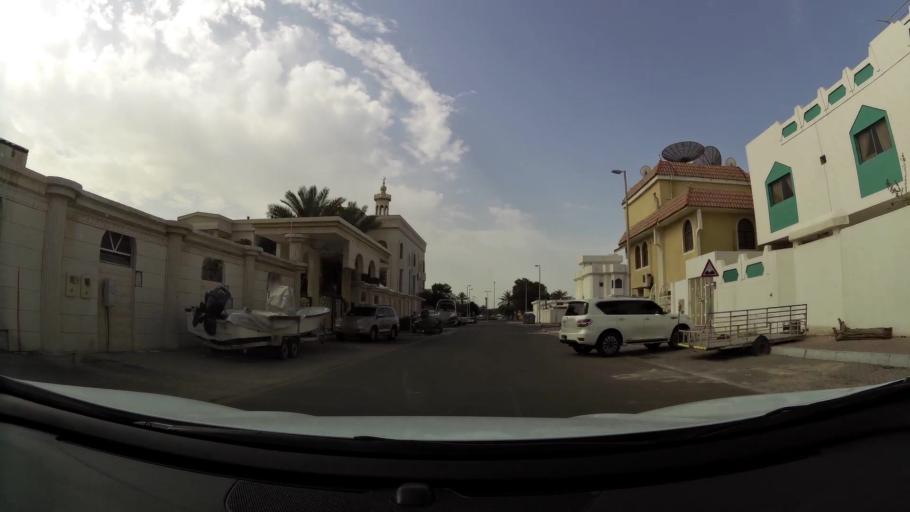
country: AE
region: Abu Dhabi
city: Abu Dhabi
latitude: 24.4391
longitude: 54.3687
